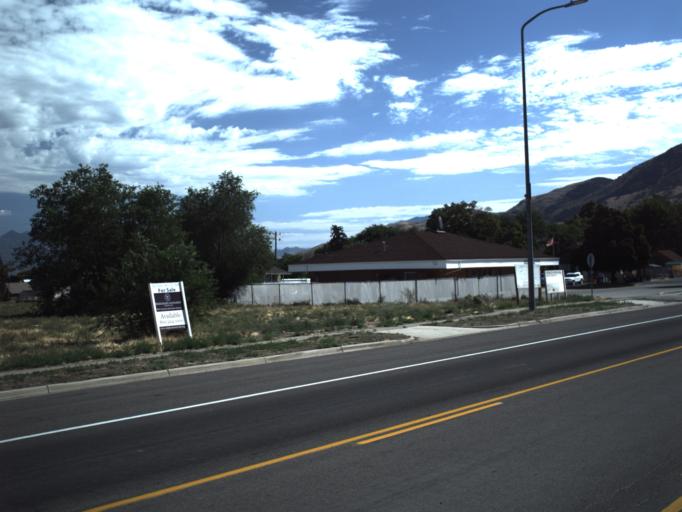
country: US
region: Utah
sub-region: Utah County
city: Santaquin
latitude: 39.9756
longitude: -111.7866
